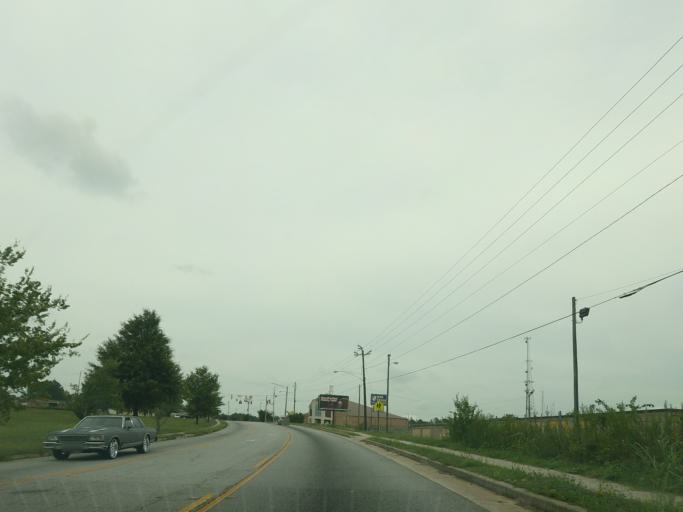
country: US
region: Georgia
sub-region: Bibb County
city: Macon
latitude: 32.8204
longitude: -83.6758
